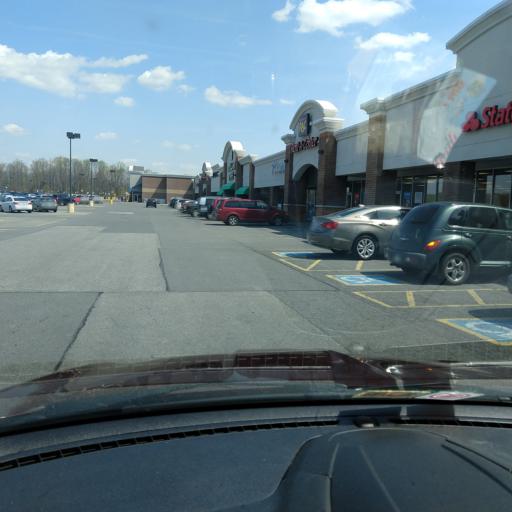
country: US
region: West Virginia
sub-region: Fayette County
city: Fayetteville
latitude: 38.0325
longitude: -81.1204
